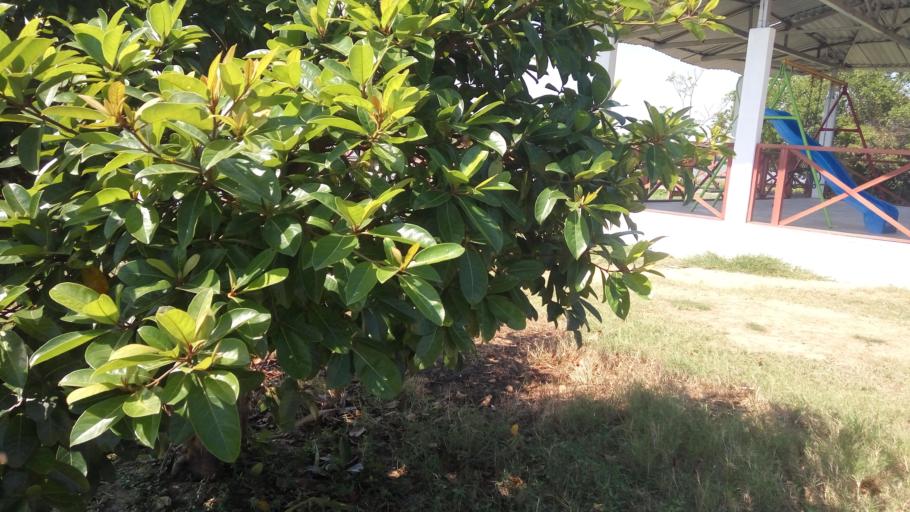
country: MX
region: Tabasco
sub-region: Centla
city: Ignacio Zaragoza
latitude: 18.3987
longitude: -92.9568
